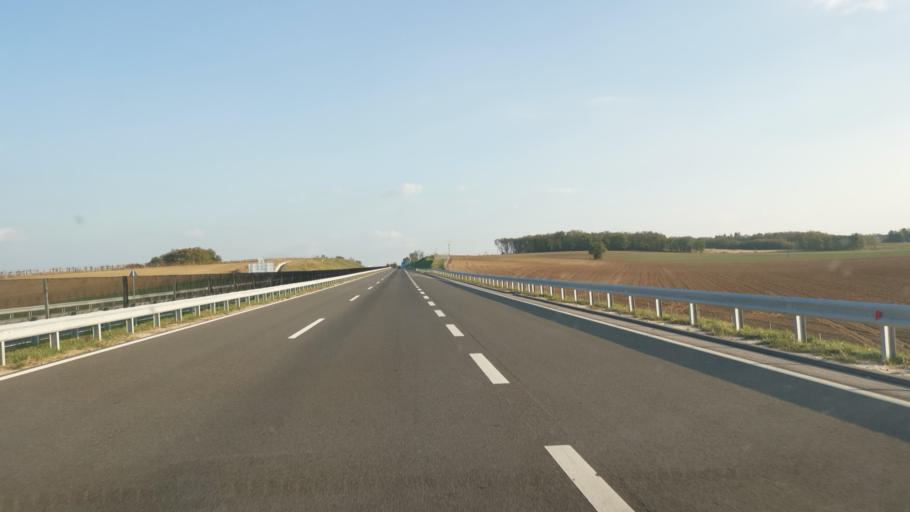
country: HU
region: Gyor-Moson-Sopron
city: Fertoszentmiklos
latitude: 47.5635
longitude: 16.8617
